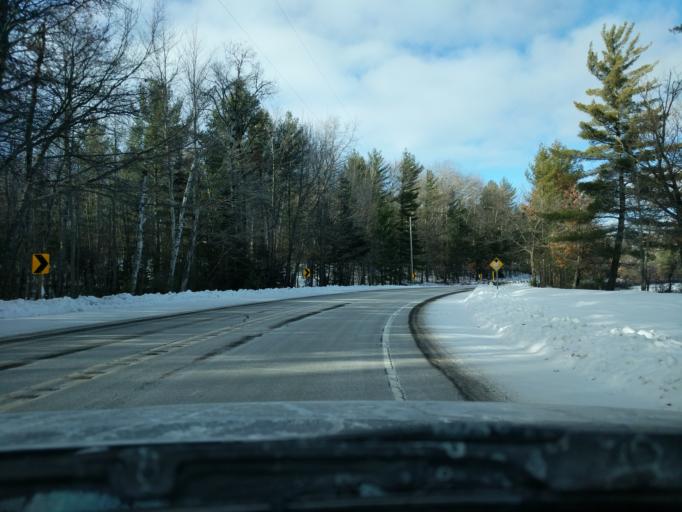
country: US
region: Wisconsin
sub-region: Vilas County
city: Eagle River
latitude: 45.7748
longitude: -89.0754
